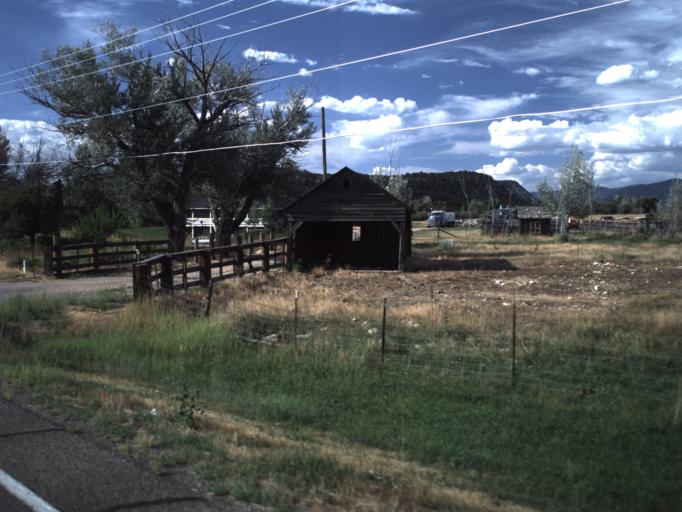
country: US
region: Utah
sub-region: Sanpete County
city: Fairview
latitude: 39.6370
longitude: -111.4448
